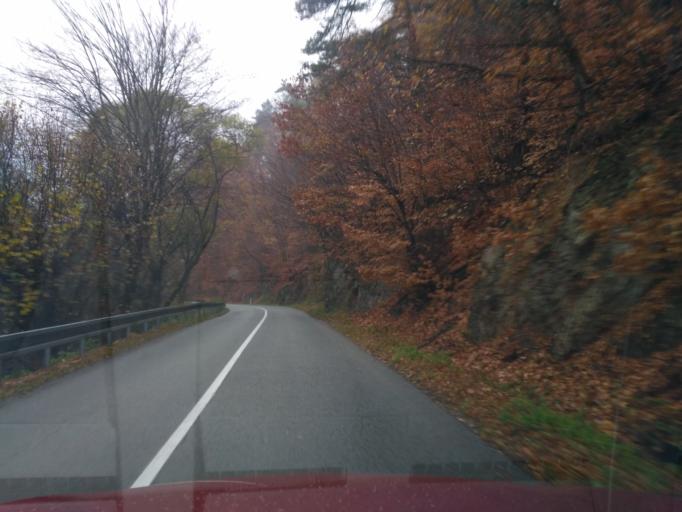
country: SK
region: Kosicky
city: Medzev
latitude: 48.7074
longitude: 20.8098
